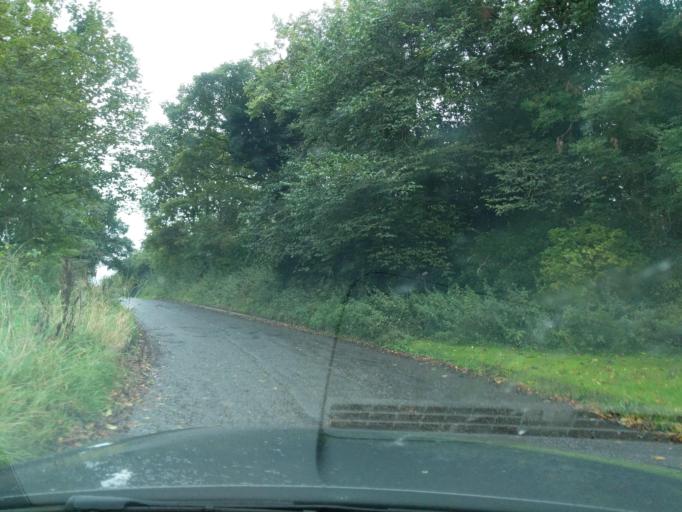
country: GB
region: Scotland
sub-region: Edinburgh
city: Balerno
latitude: 55.9061
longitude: -3.3414
